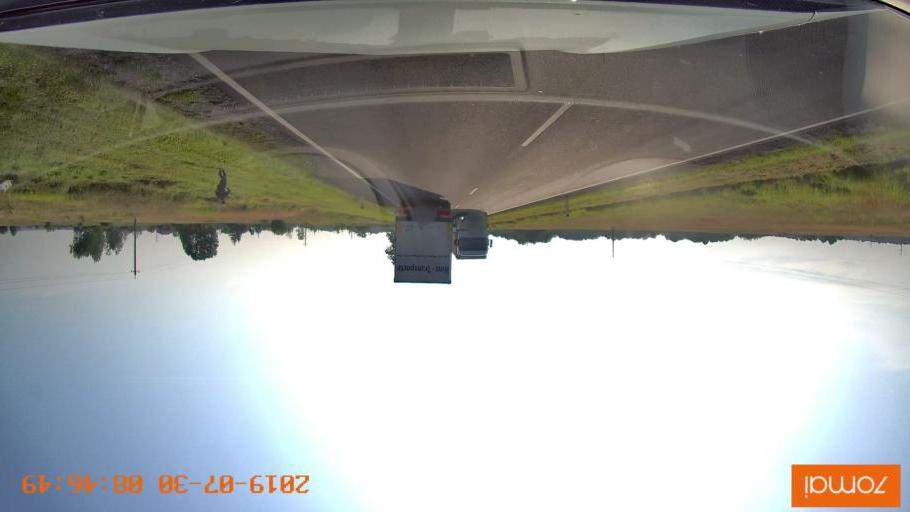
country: RU
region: Kaliningrad
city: Chernyakhovsk
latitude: 54.6217
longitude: 21.8917
